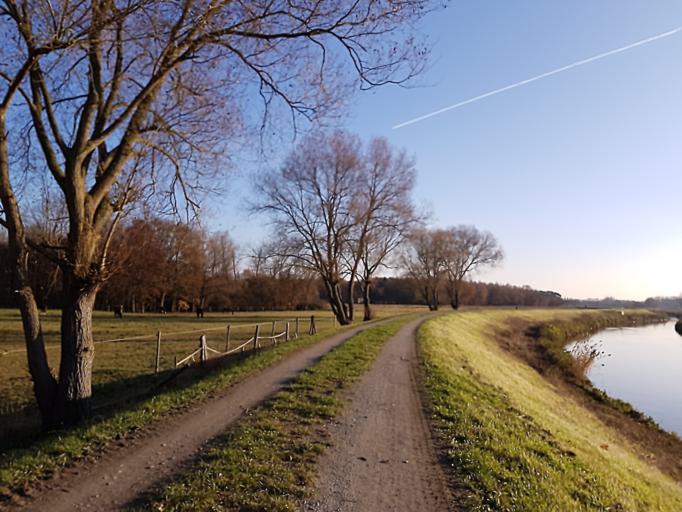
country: BE
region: Flanders
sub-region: Provincie Vlaams-Brabant
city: Boortmeerbeek
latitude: 50.9993
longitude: 4.5982
